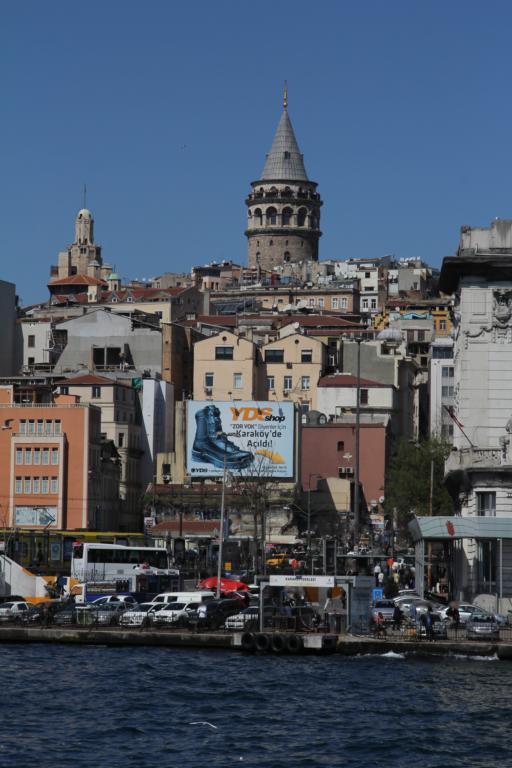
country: TR
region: Istanbul
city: Eminoenue
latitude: 41.0225
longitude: 28.9803
